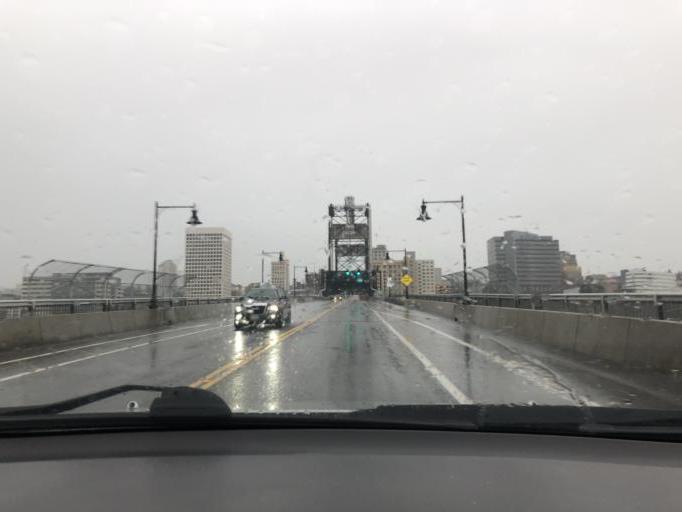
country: US
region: Washington
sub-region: Pierce County
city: Tacoma
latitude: 47.2543
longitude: -122.4302
